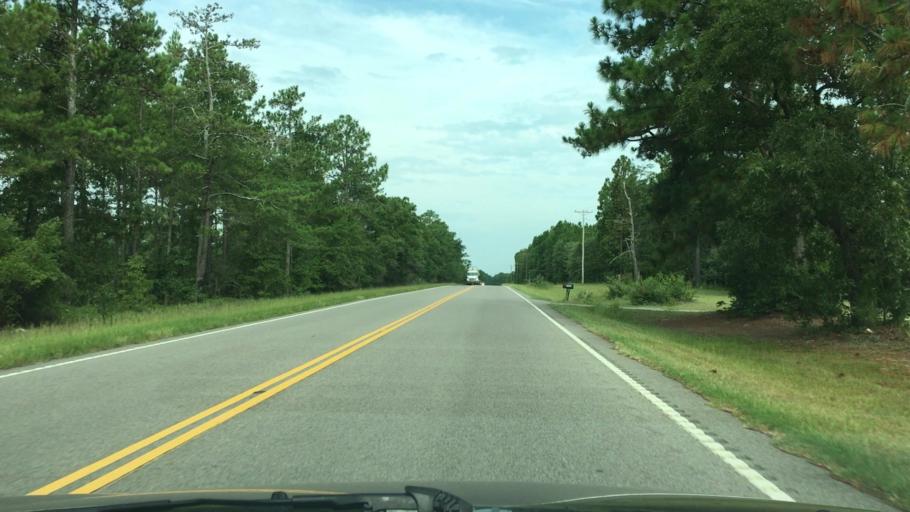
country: US
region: South Carolina
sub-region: Lexington County
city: Leesville
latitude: 33.6735
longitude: -81.4205
